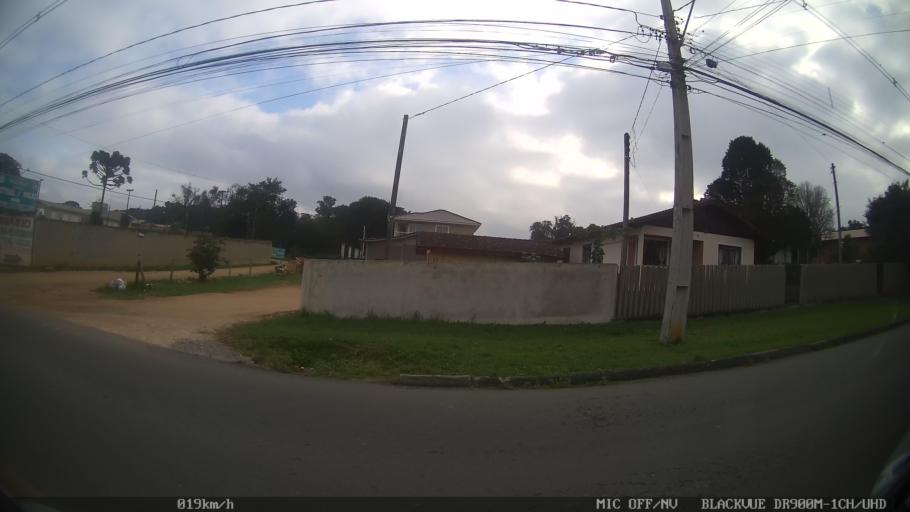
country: BR
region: Parana
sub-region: Curitiba
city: Curitiba
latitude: -25.3932
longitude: -49.3277
